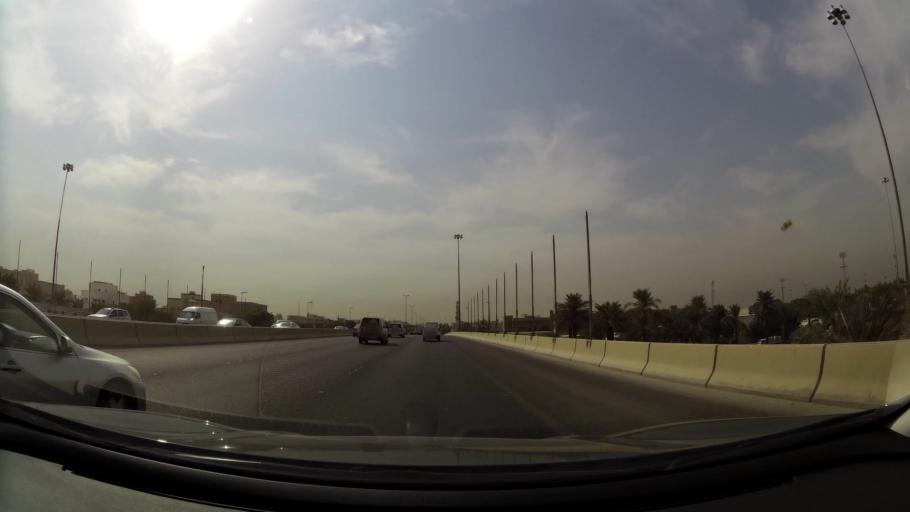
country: KW
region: Al Asimah
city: Ash Shamiyah
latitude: 29.3439
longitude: 47.9723
